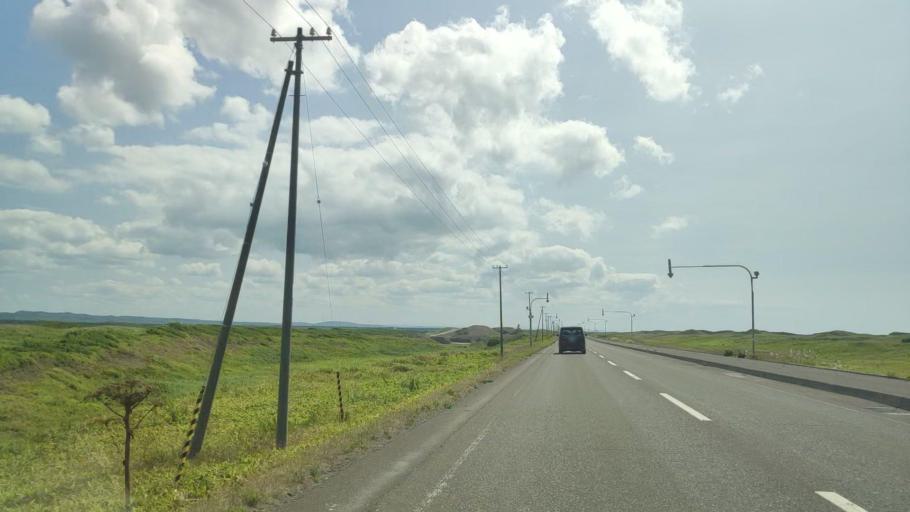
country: JP
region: Hokkaido
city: Makubetsu
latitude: 44.9441
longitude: 141.7138
